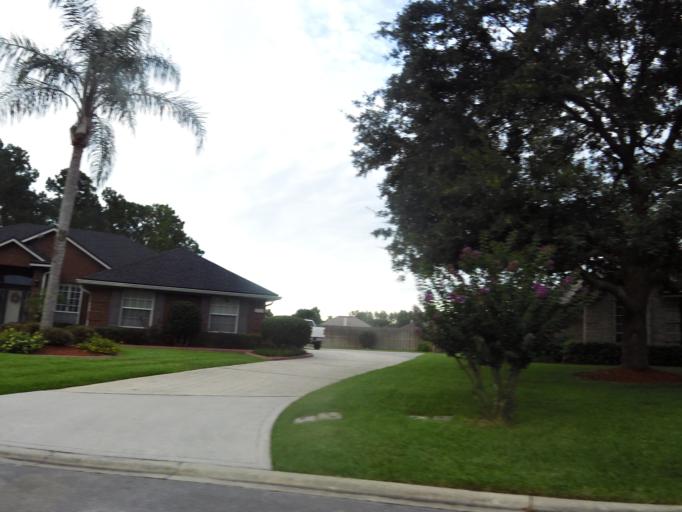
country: US
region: Florida
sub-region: Duval County
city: Baldwin
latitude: 30.3065
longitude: -81.8258
